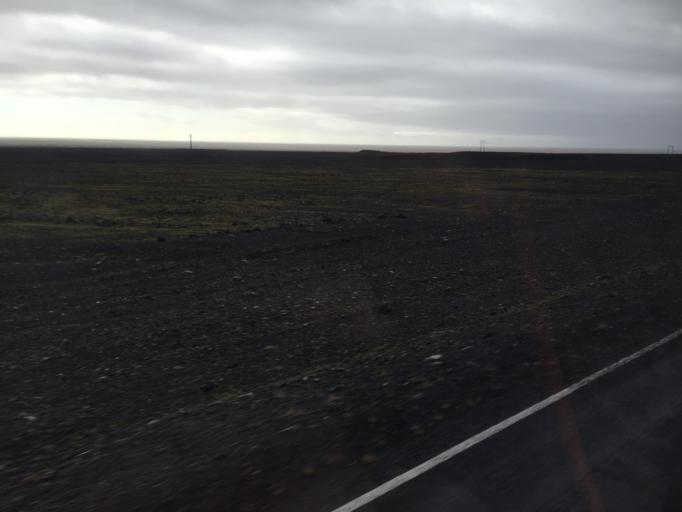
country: IS
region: East
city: Hoefn
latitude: 63.9195
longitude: -16.7754
